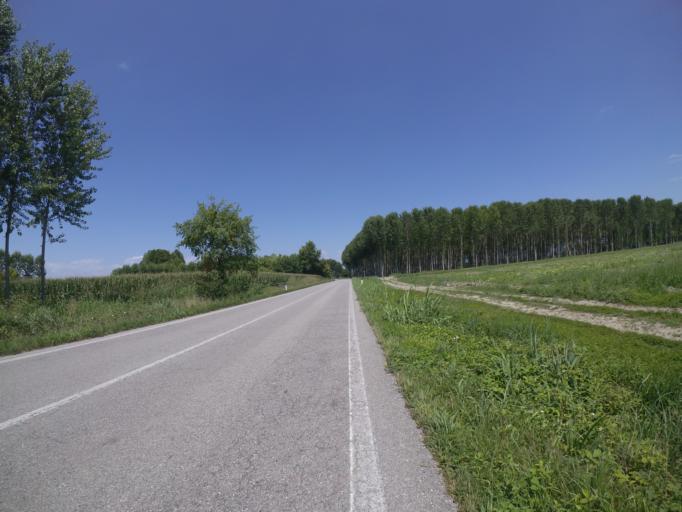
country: IT
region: Friuli Venezia Giulia
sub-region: Provincia di Udine
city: Talmassons
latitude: 45.9103
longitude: 13.1369
